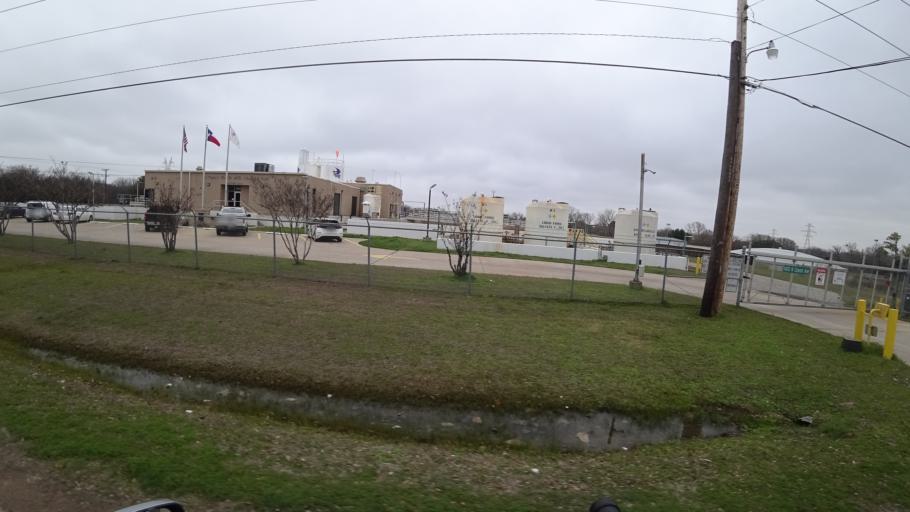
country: US
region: Texas
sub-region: Denton County
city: Lewisville
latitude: 33.0629
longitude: -97.0012
